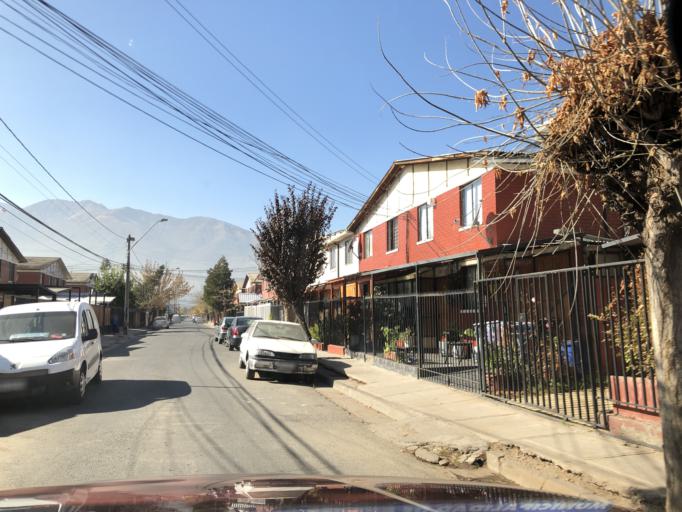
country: CL
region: Santiago Metropolitan
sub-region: Provincia de Cordillera
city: Puente Alto
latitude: -33.5655
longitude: -70.5768
